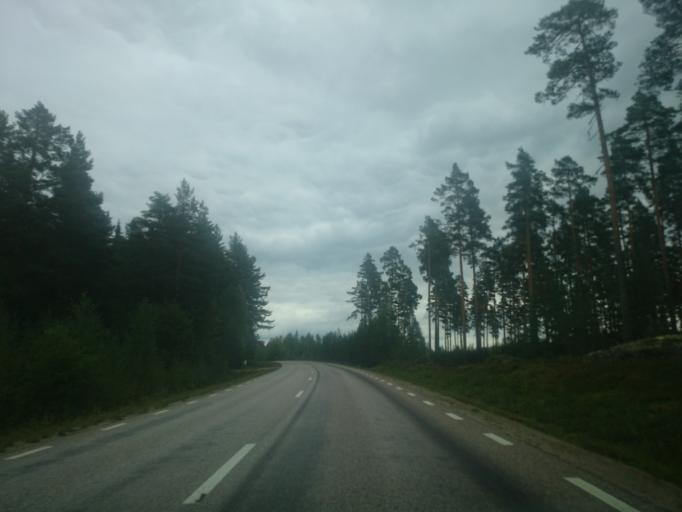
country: SE
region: Gaevleborg
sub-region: Ljusdals Kommun
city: Farila
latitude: 61.9878
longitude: 15.2821
